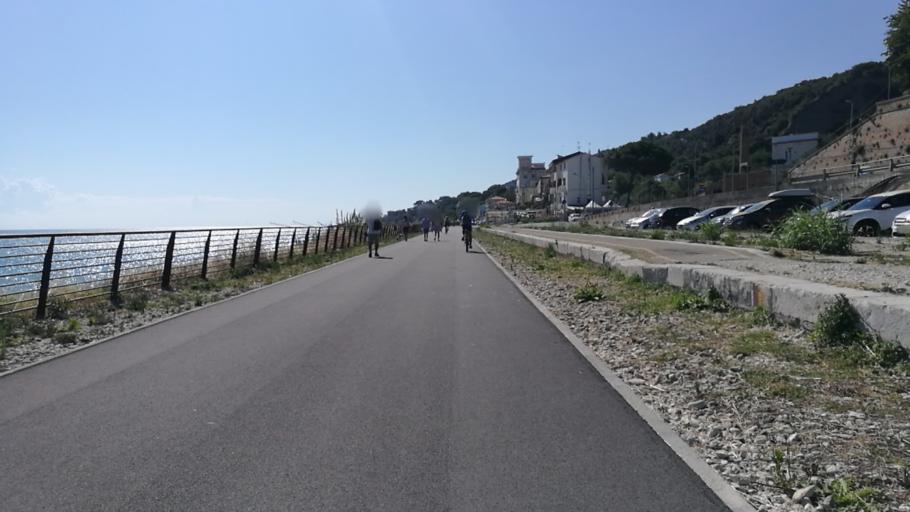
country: IT
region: Abruzzo
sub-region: Provincia di Chieti
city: Marina di San Vito
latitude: 42.3072
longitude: 14.4486
